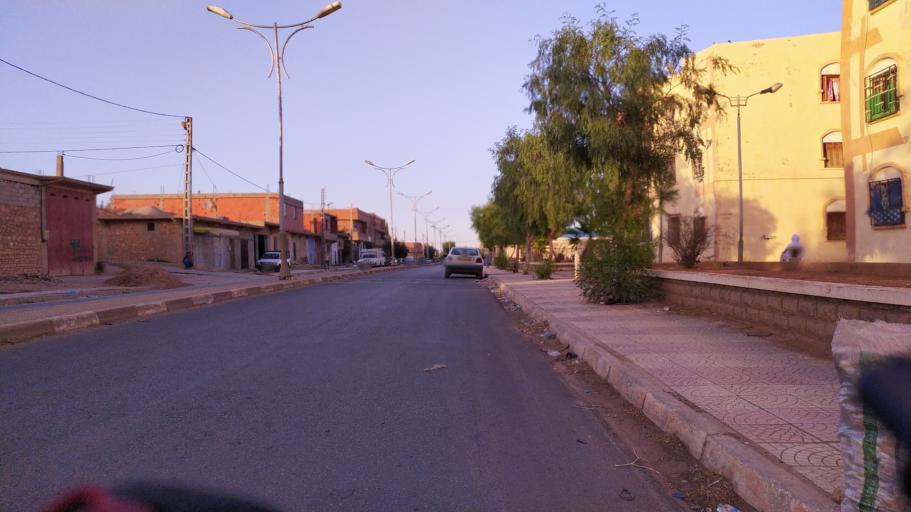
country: DZ
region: Tiaret
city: Frenda
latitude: 34.8893
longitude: 1.2429
